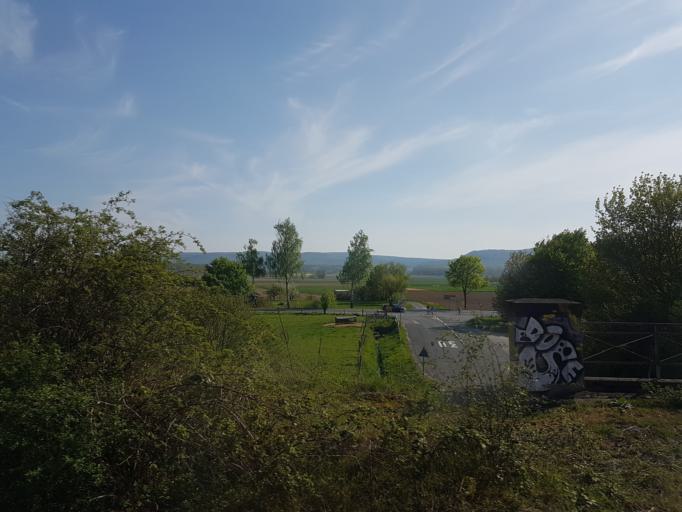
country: DE
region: Lower Saxony
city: Springe
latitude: 52.2121
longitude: 9.6199
